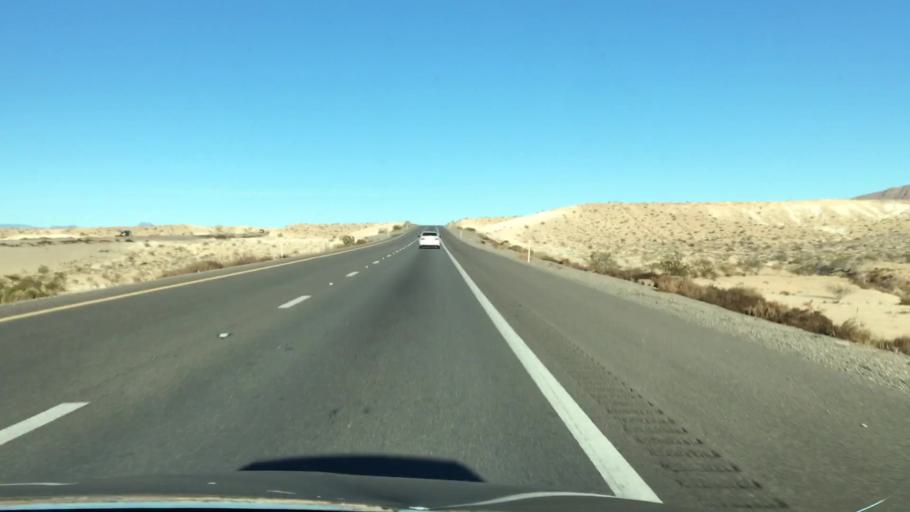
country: US
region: Nevada
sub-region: Clark County
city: Moapa Town
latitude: 36.5666
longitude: -114.6755
